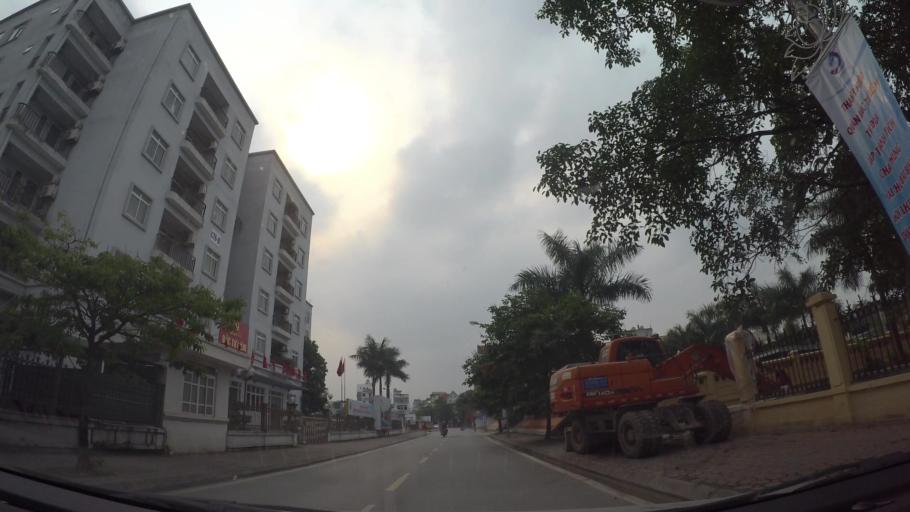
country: VN
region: Ha Noi
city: Cau Dien
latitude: 21.0427
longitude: 105.7536
